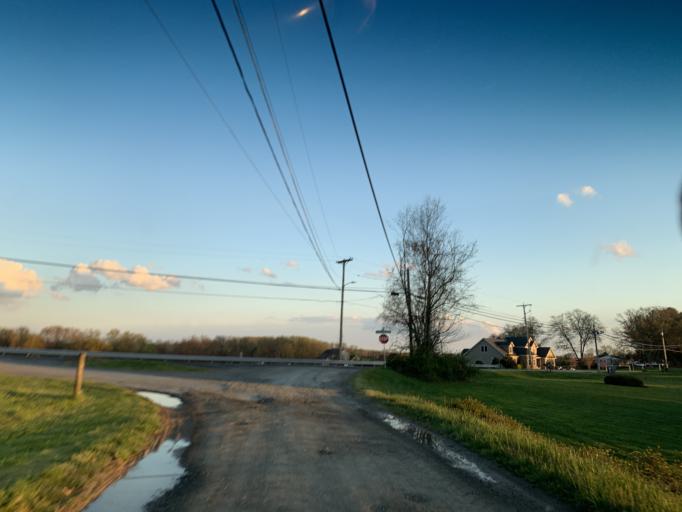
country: US
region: Maryland
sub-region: Harford County
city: Bel Air North
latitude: 39.6137
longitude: -76.3582
